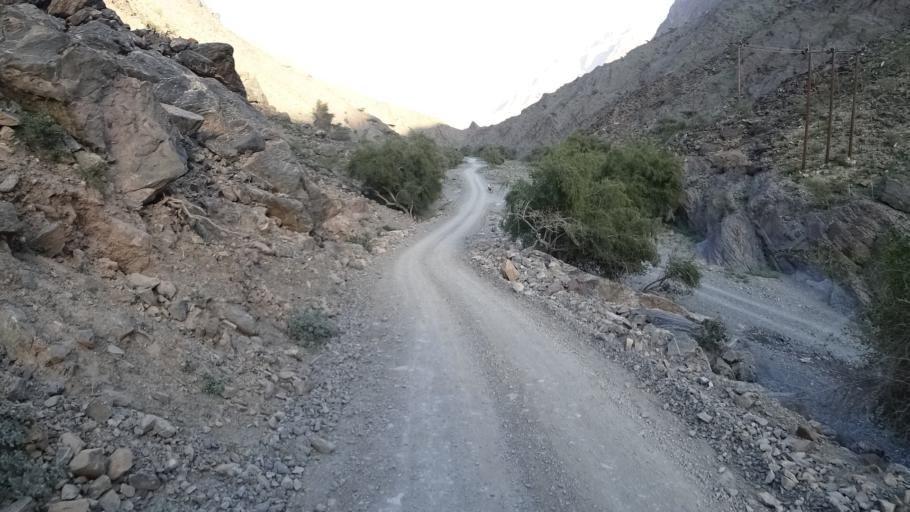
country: OM
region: Al Batinah
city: Bayt al `Awabi
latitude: 23.2548
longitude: 57.4069
